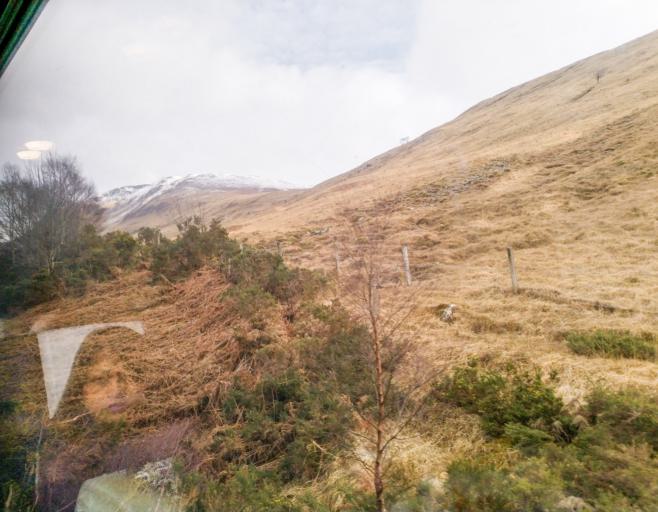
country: GB
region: Scotland
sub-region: Highland
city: Spean Bridge
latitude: 56.8078
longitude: -4.7183
